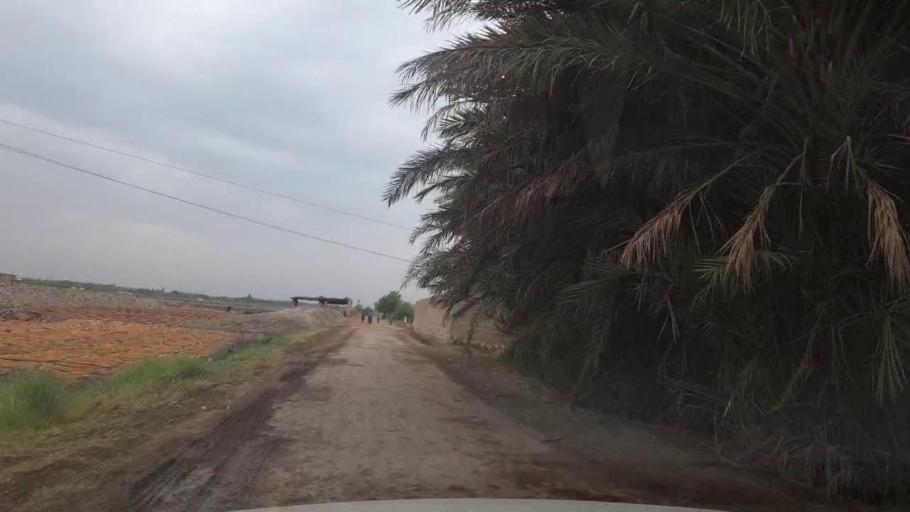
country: PK
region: Sindh
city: Khairpur
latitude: 27.5914
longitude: 68.8134
